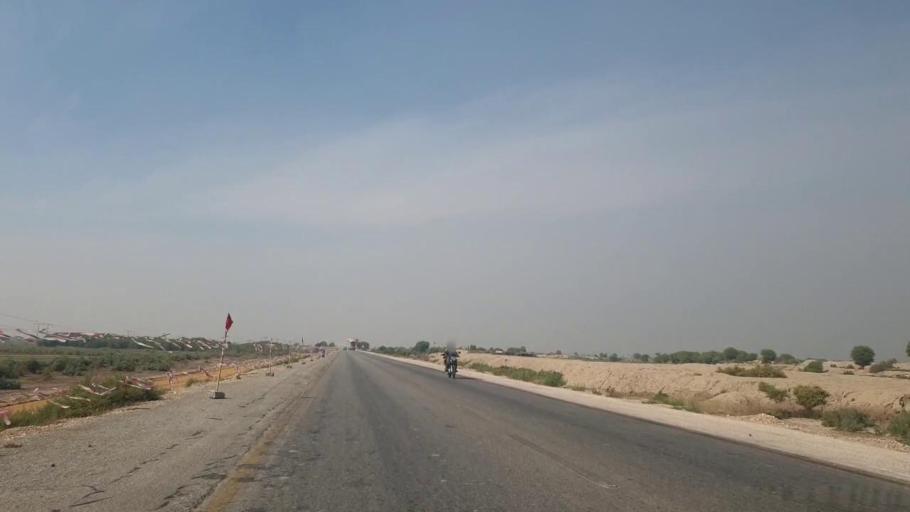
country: PK
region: Sindh
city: Sann
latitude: 25.9933
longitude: 68.1720
